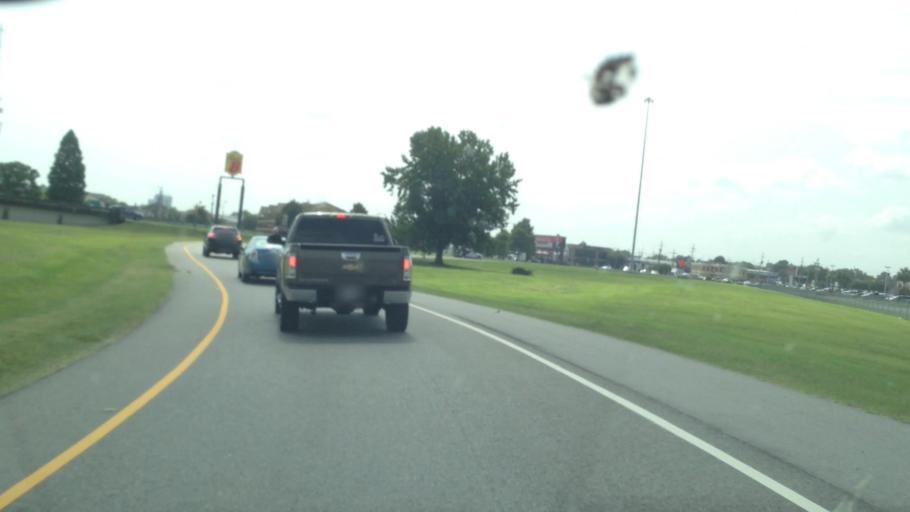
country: US
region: Louisiana
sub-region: Jefferson Parish
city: Metairie Terrace
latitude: 29.9972
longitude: -90.1855
